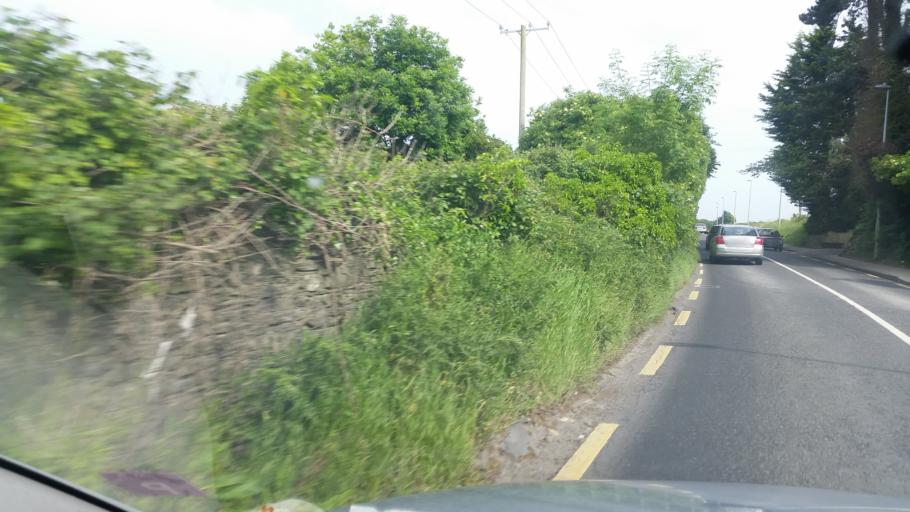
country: IE
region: Leinster
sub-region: Dublin City
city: Finglas
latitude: 53.4104
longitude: -6.3061
